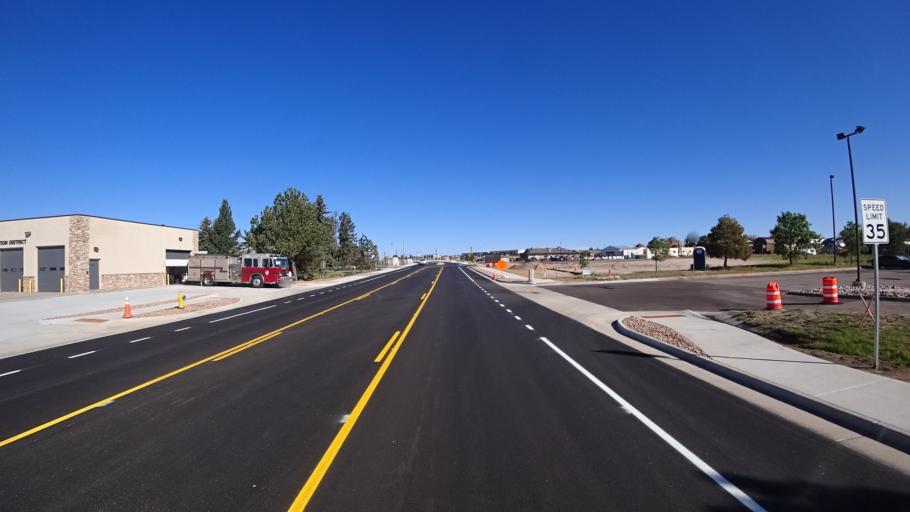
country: US
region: Colorado
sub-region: El Paso County
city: Cimarron Hills
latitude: 38.9338
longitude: -104.6090
